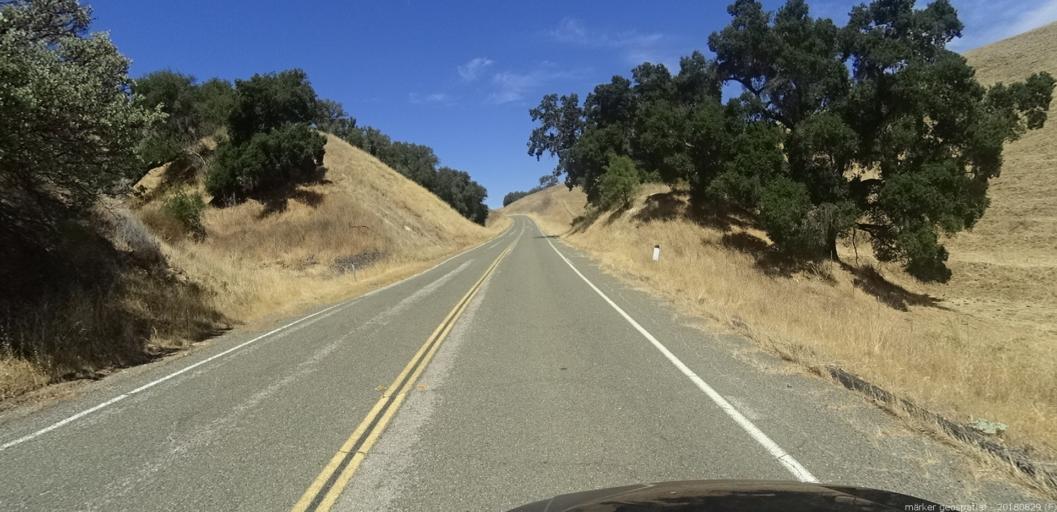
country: US
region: California
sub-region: San Luis Obispo County
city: Lake Nacimiento
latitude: 35.8426
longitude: -121.0454
